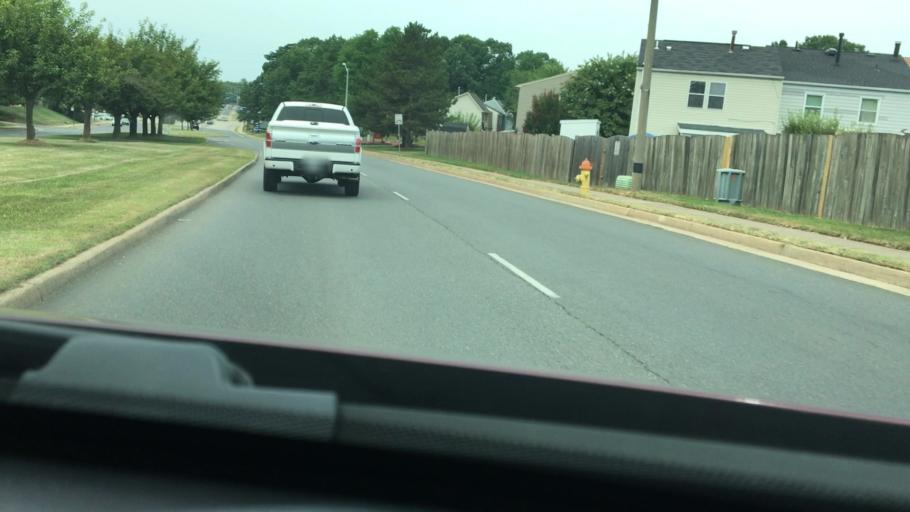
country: US
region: Virginia
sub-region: Prince William County
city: Yorkshire
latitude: 38.7712
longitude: -77.4486
